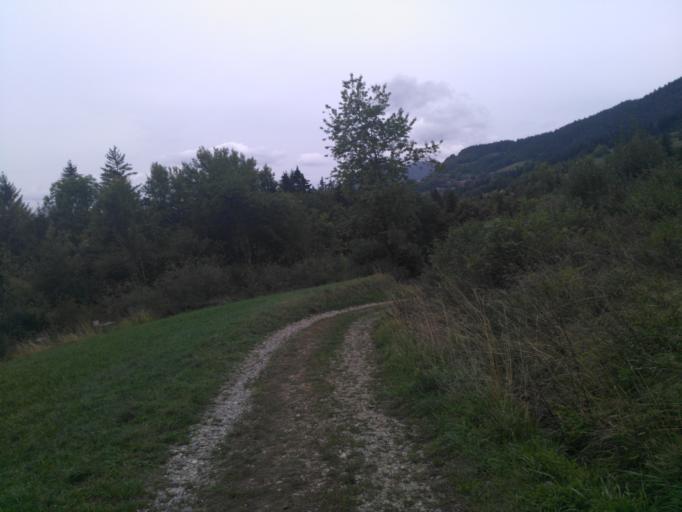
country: FR
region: Rhone-Alpes
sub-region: Departement de la Haute-Savoie
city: Talloires
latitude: 45.8316
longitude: 6.2350
